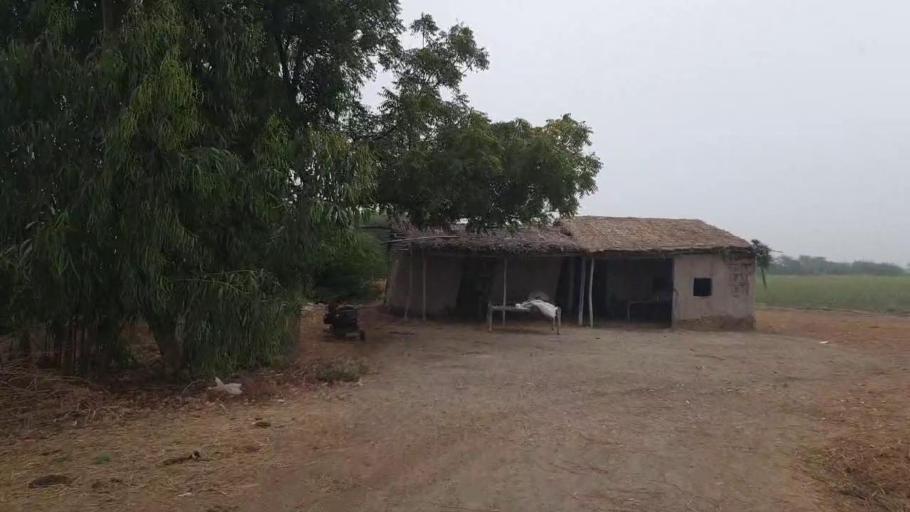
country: PK
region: Sindh
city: Badin
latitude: 24.6214
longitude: 68.6918
